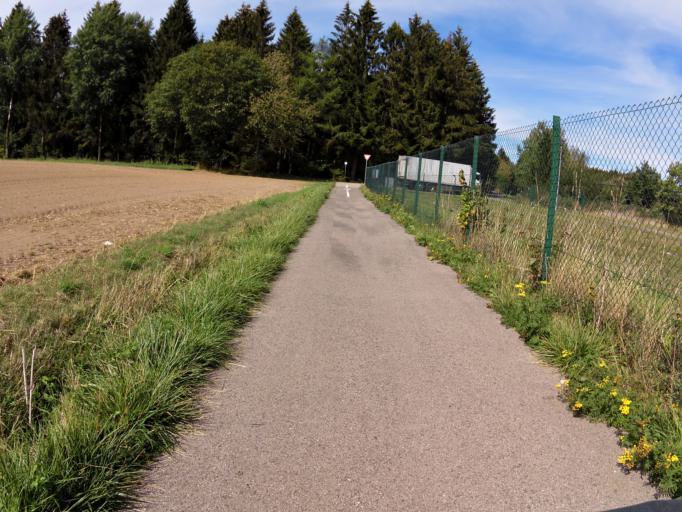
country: DE
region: Rheinland-Pfalz
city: Arzfeld
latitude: 50.0943
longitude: 6.2723
